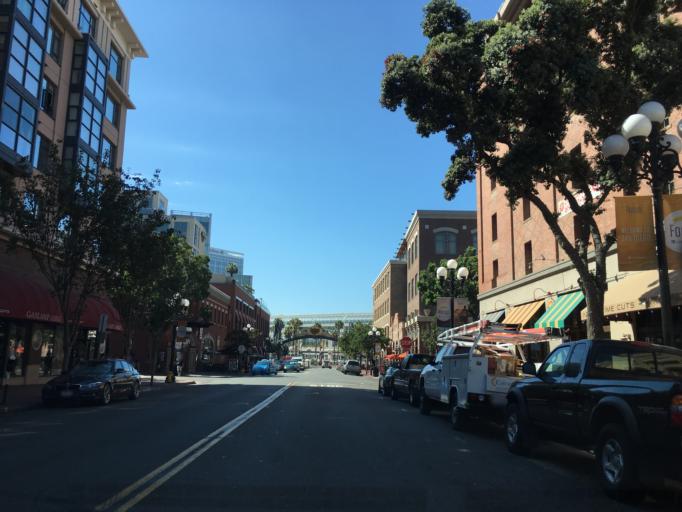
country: US
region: California
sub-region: San Diego County
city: San Diego
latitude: 32.7089
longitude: -117.1601
